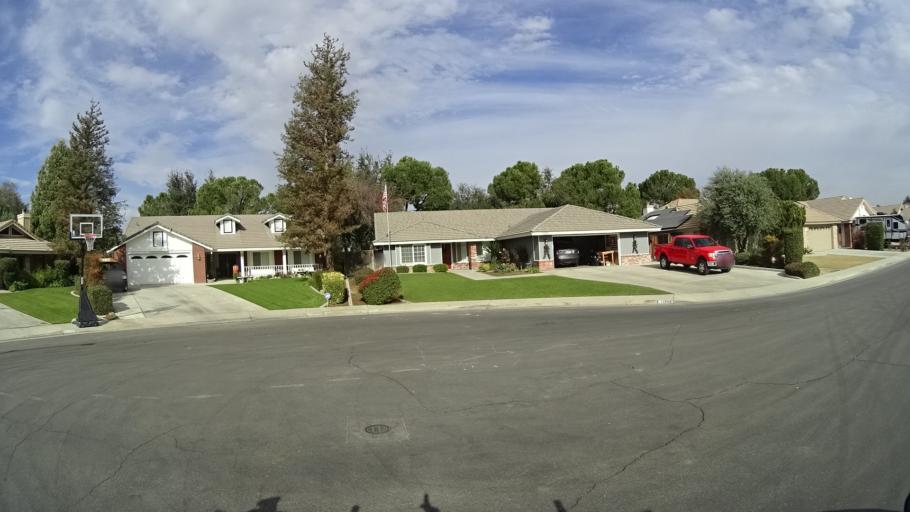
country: US
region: California
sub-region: Kern County
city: Greenacres
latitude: 35.4118
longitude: -119.1269
